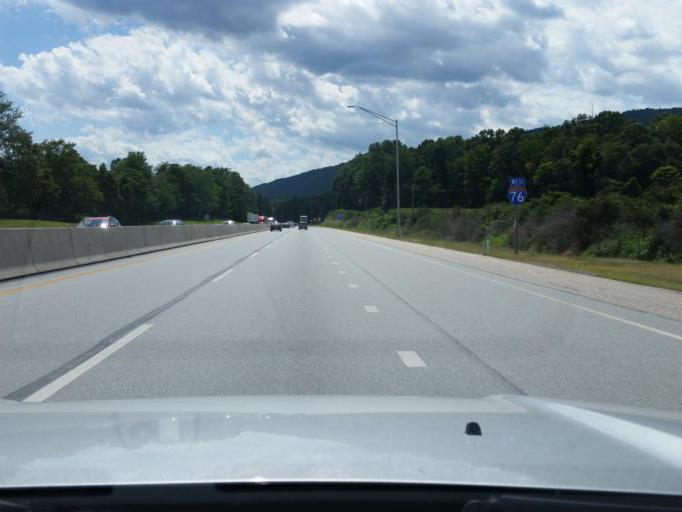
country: US
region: Pennsylvania
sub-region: Franklin County
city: Doylestown
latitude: 40.0953
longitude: -77.8182
